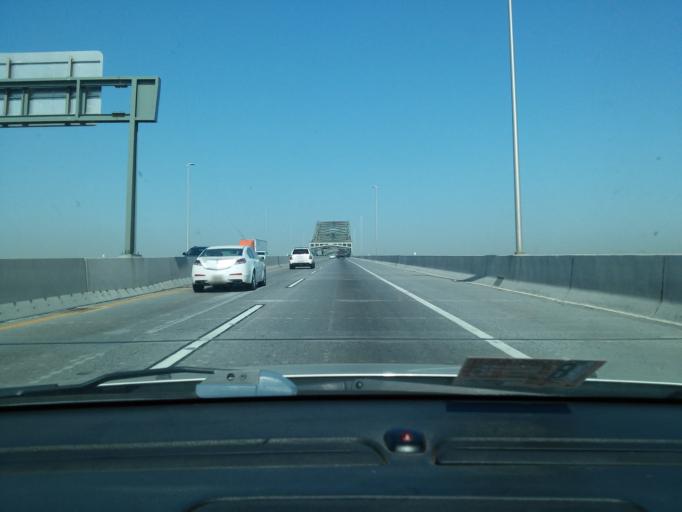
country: US
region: New Jersey
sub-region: Hudson County
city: Bayonne
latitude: 40.6944
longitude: -74.1151
